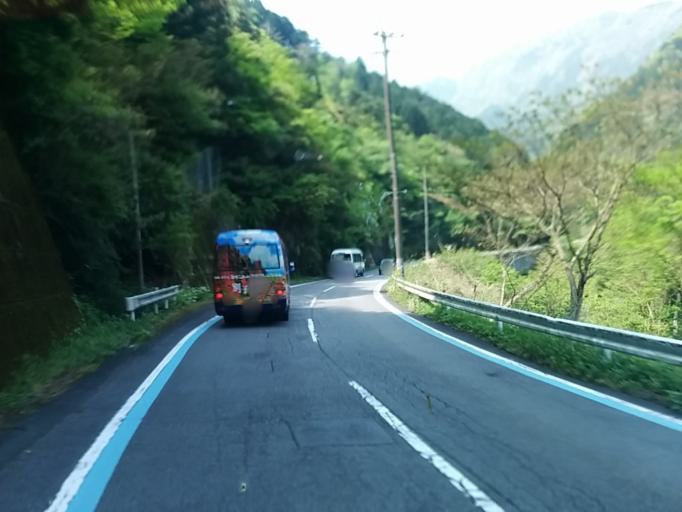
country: JP
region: Ehime
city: Niihama
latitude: 33.8843
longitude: 133.3038
